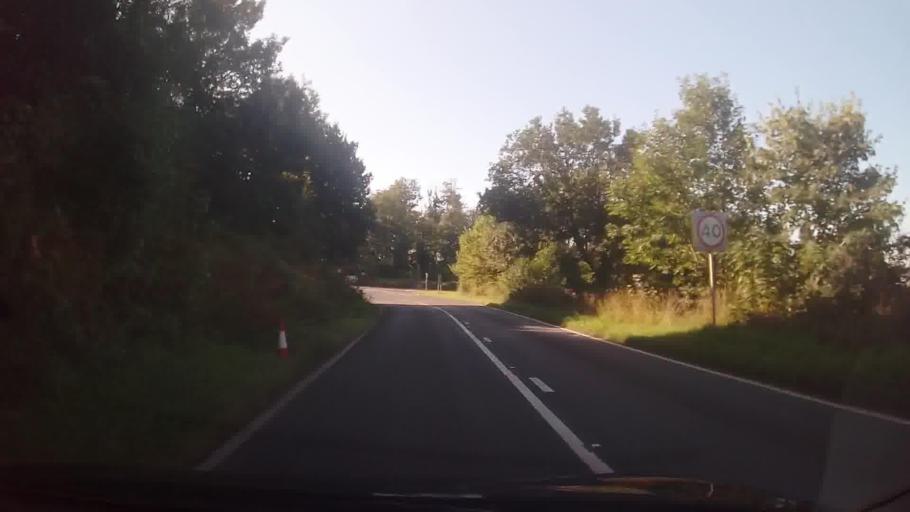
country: GB
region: England
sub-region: Cumbria
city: Seascale
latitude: 54.3586
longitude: -3.3990
